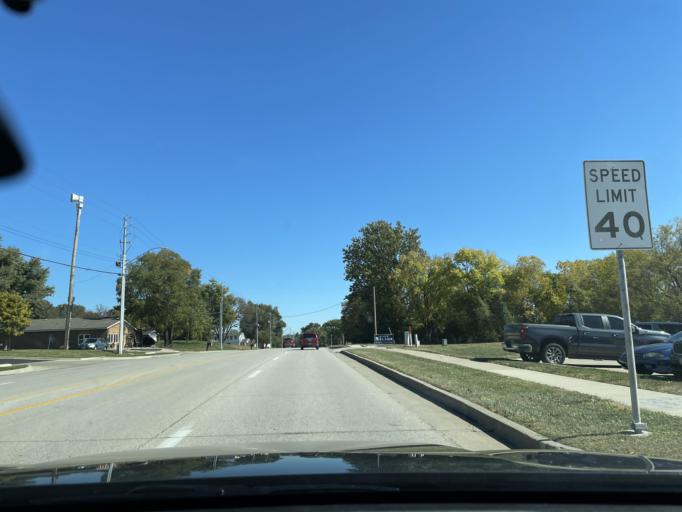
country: US
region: Missouri
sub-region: Andrew County
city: Country Club Village
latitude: 39.7804
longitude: -94.7773
